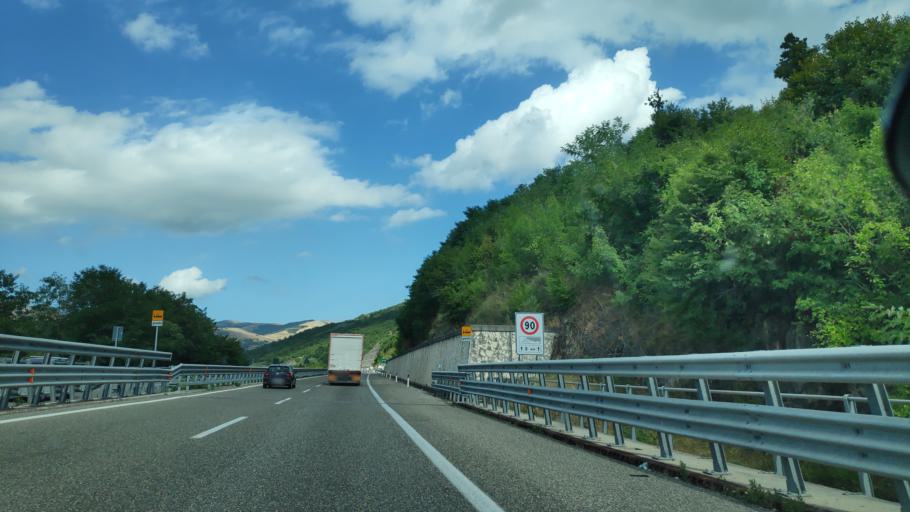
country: IT
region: Campania
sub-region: Provincia di Salerno
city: Pertosa
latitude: 40.5318
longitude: 15.4433
